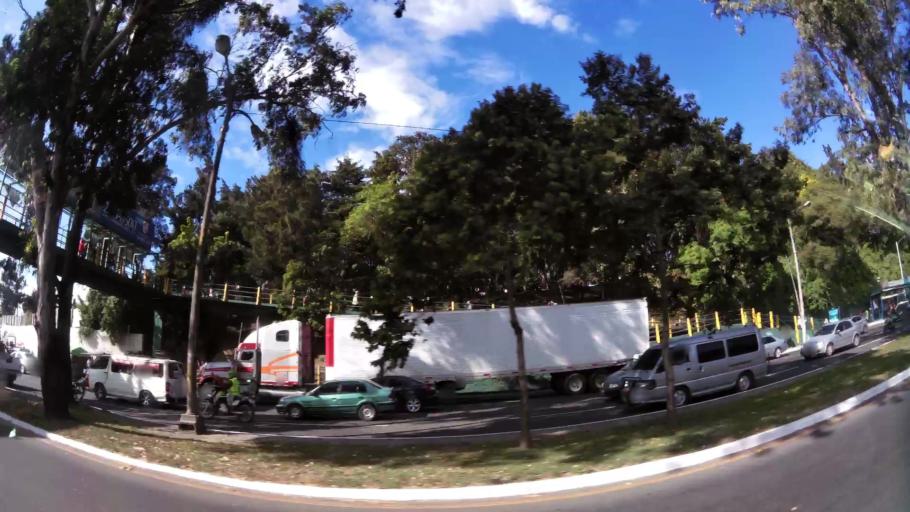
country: GT
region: Guatemala
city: Guatemala City
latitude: 14.6083
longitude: -90.5317
